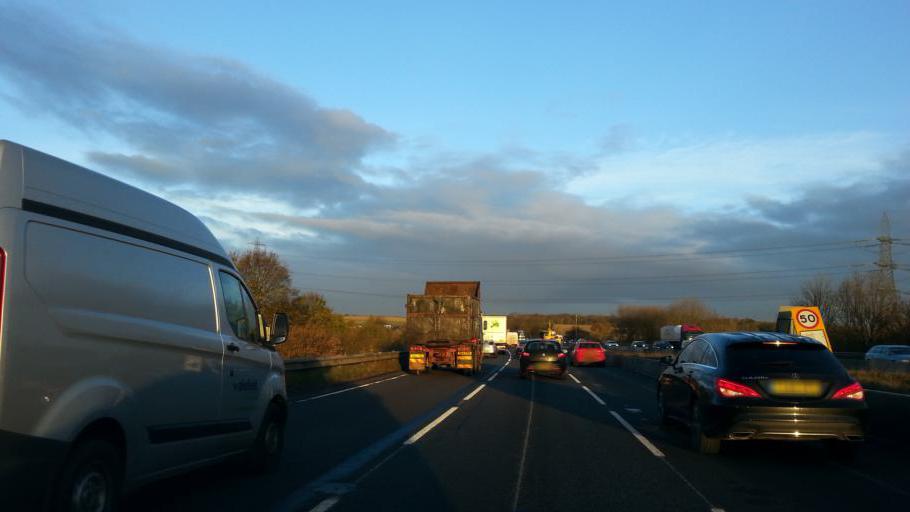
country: GB
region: England
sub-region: City and Borough of Wakefield
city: Normanton
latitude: 53.7237
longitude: -1.4311
